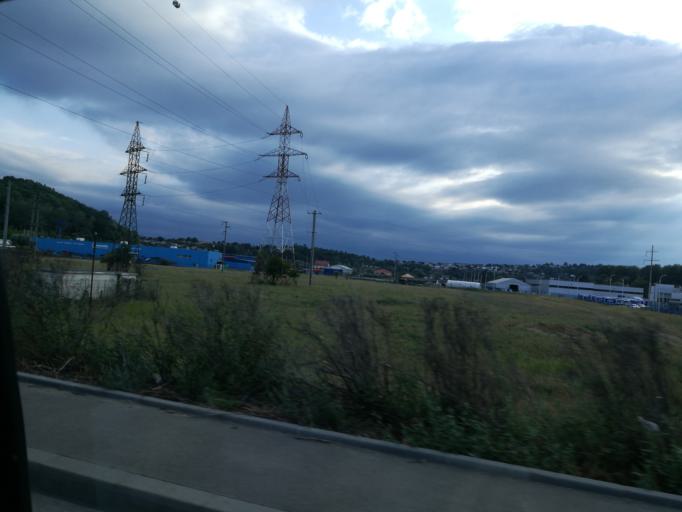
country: RO
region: Suceava
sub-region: Comuna Scheia
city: Scheia
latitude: 47.6688
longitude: 26.2433
